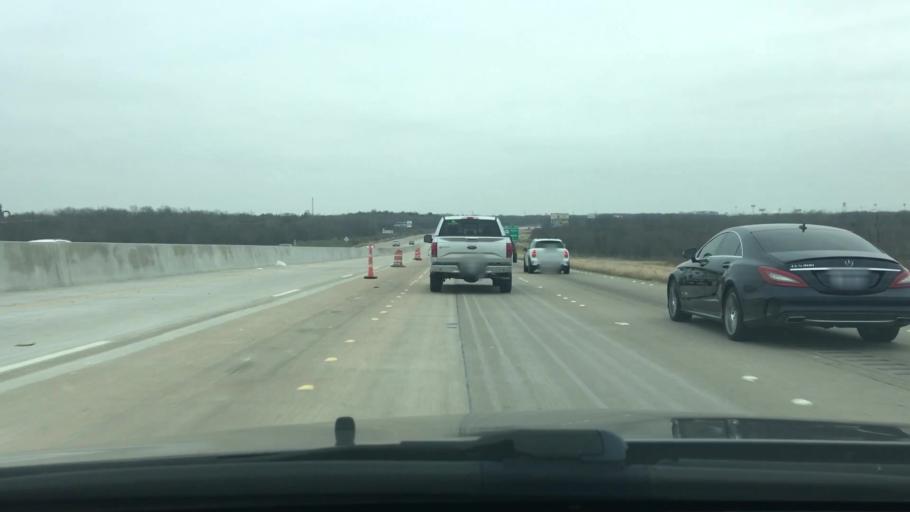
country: US
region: Texas
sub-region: Navarro County
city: Corsicana
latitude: 32.0924
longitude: -96.4400
